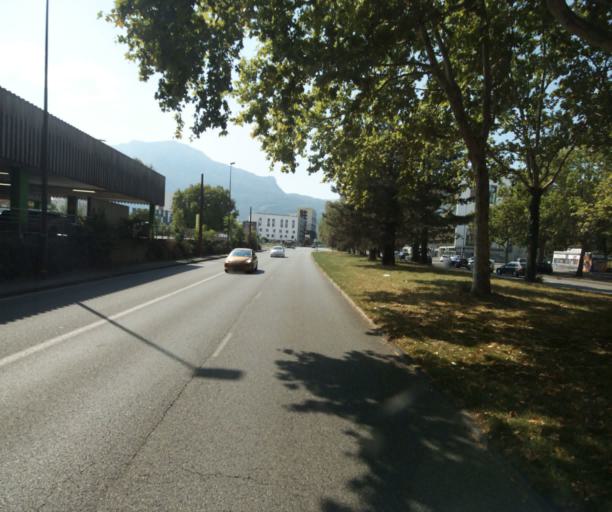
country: FR
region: Rhone-Alpes
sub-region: Departement de l'Isere
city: Grenoble
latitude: 45.1592
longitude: 5.7253
